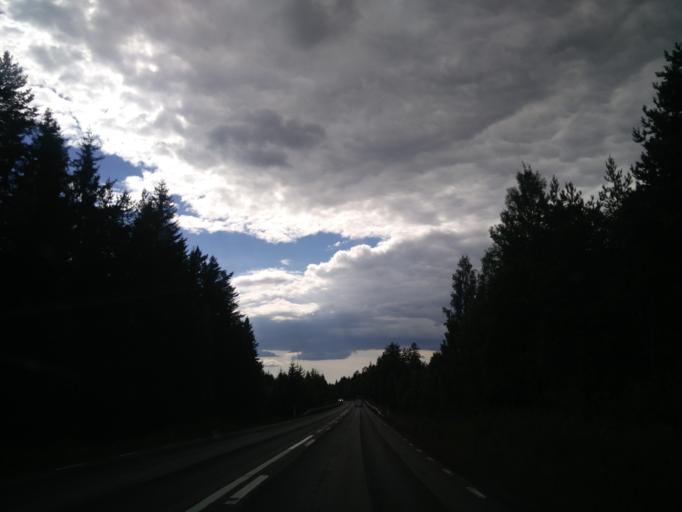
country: SE
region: Vaermland
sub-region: Filipstads Kommun
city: Filipstad
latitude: 59.7759
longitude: 14.2918
